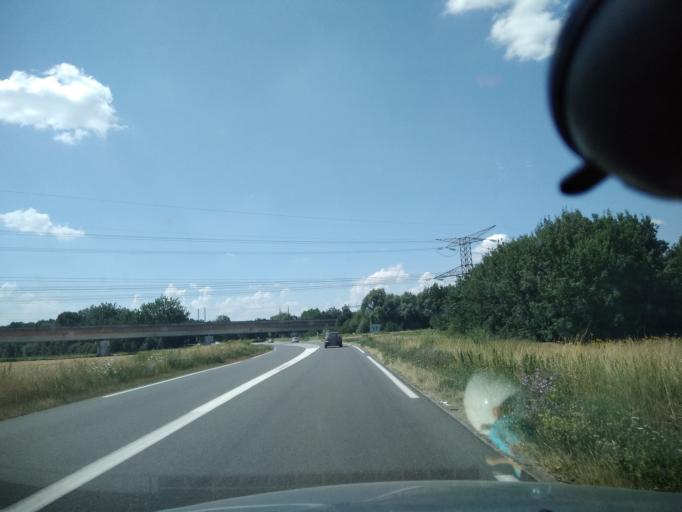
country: FR
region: Centre
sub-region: Departement d'Indre-et-Loire
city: Larcay
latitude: 47.3799
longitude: 0.7914
